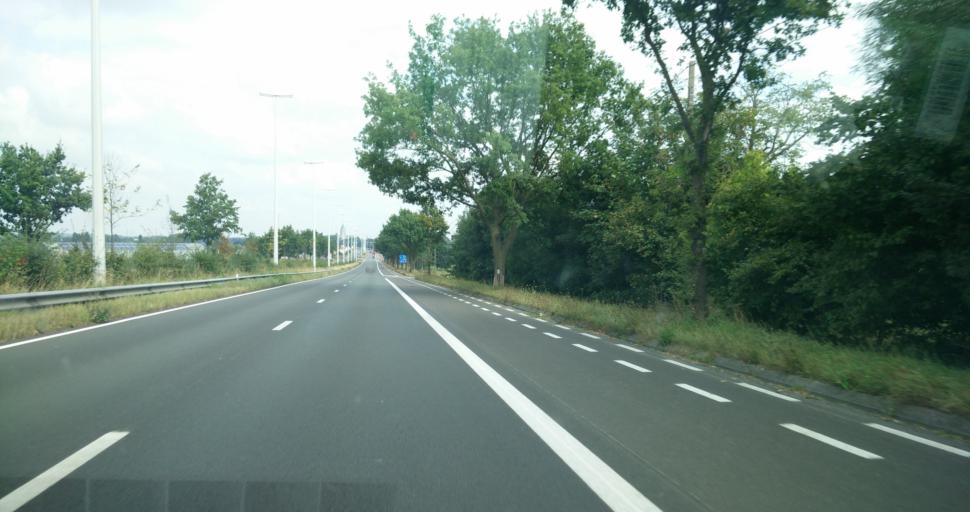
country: BE
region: Flanders
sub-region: Provincie Oost-Vlaanderen
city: Oudenaarde
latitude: 50.8185
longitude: 3.6039
